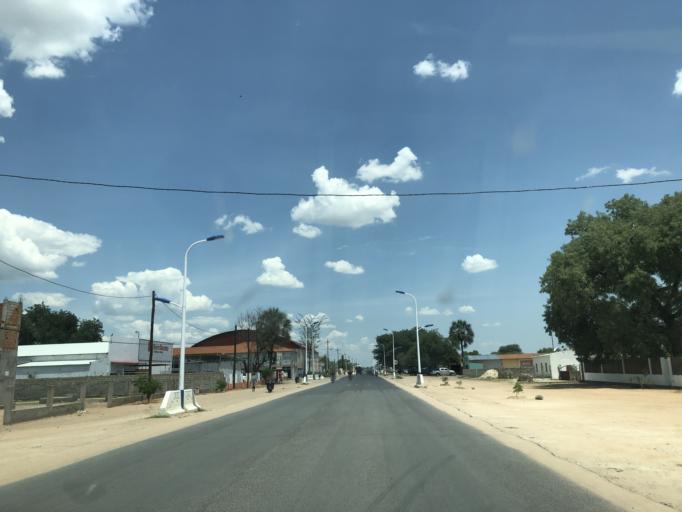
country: AO
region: Cunene
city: Ondjiva
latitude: -17.0816
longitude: 15.7385
